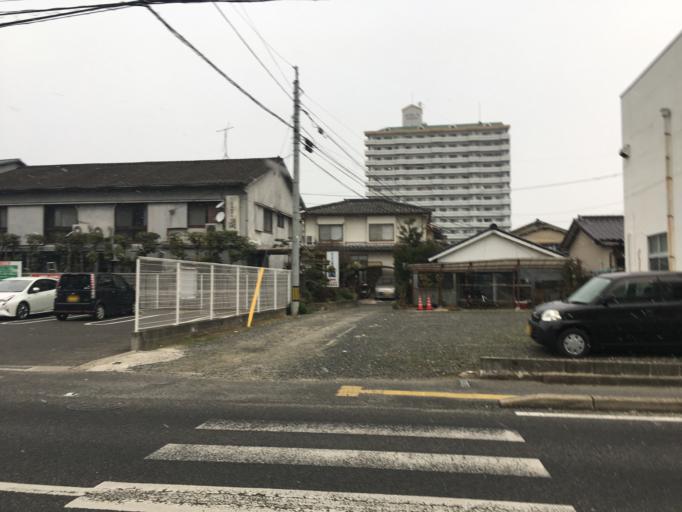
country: JP
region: Saga Prefecture
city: Saga-shi
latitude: 33.2595
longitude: 130.2947
